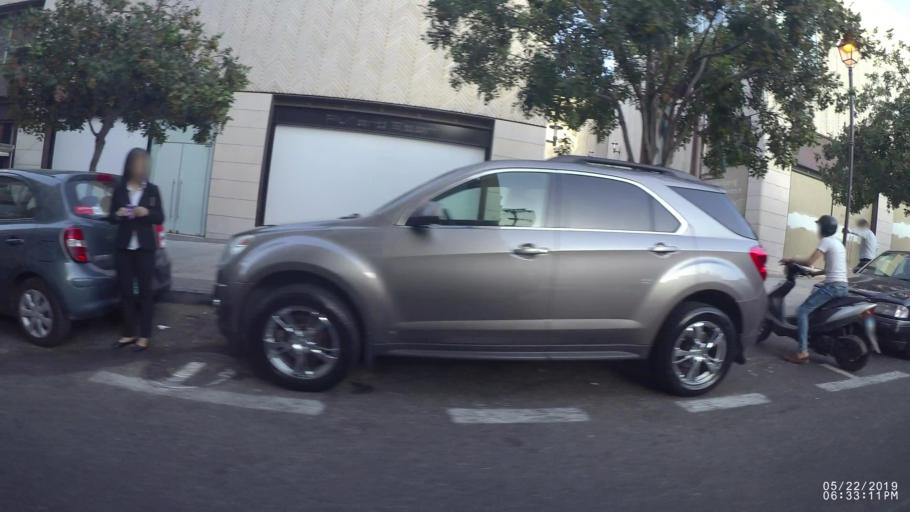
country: LB
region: Beyrouth
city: Beirut
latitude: 33.8999
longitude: 35.5029
